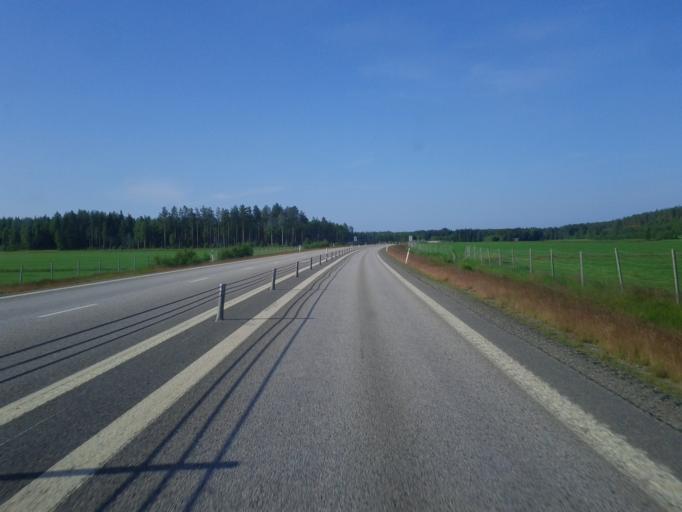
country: SE
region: Vaesterbotten
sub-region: Robertsfors Kommun
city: Robertsfors
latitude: 64.1026
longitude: 20.8718
